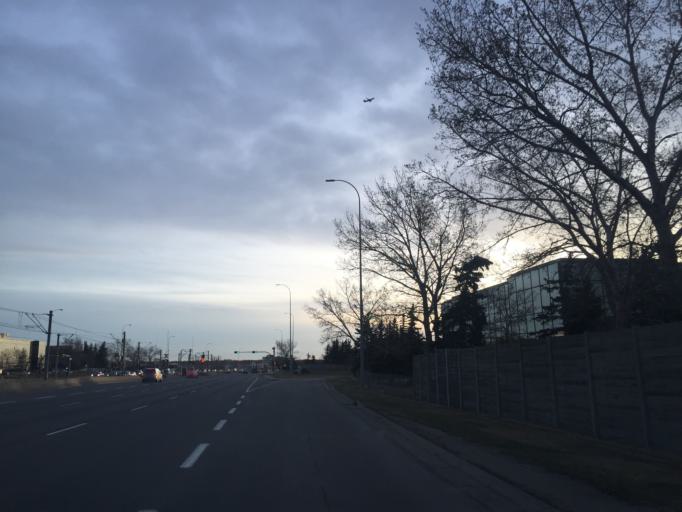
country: CA
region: Alberta
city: Calgary
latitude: 51.0480
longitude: -113.9926
